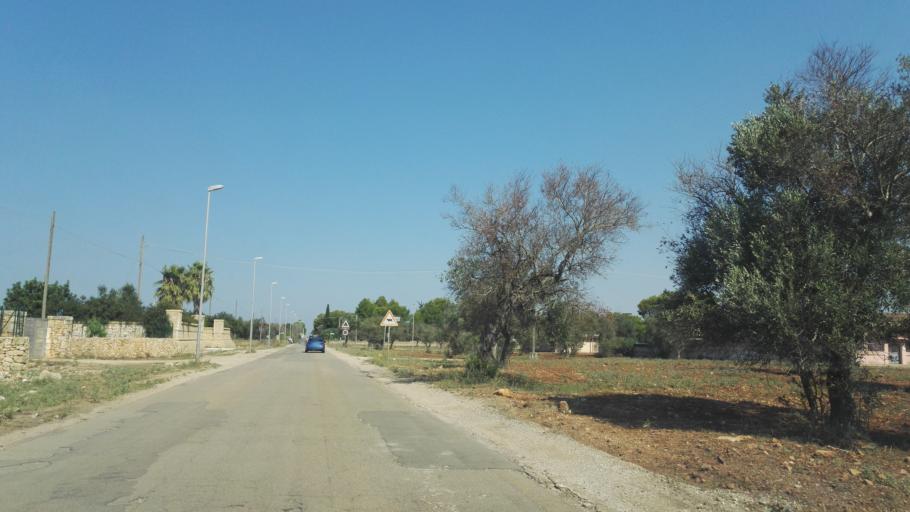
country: IT
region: Apulia
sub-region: Provincia di Lecce
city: Nardo
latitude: 40.1409
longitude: 18.0131
